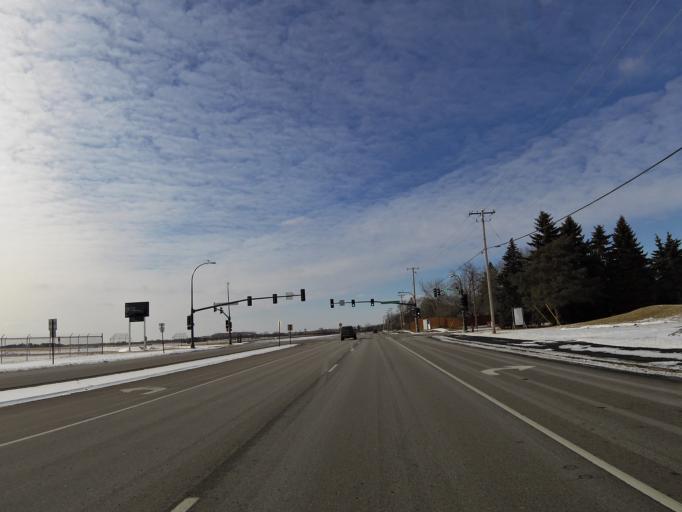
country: US
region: Minnesota
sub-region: Hennepin County
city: Eden Prairie
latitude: 44.8338
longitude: -93.4647
